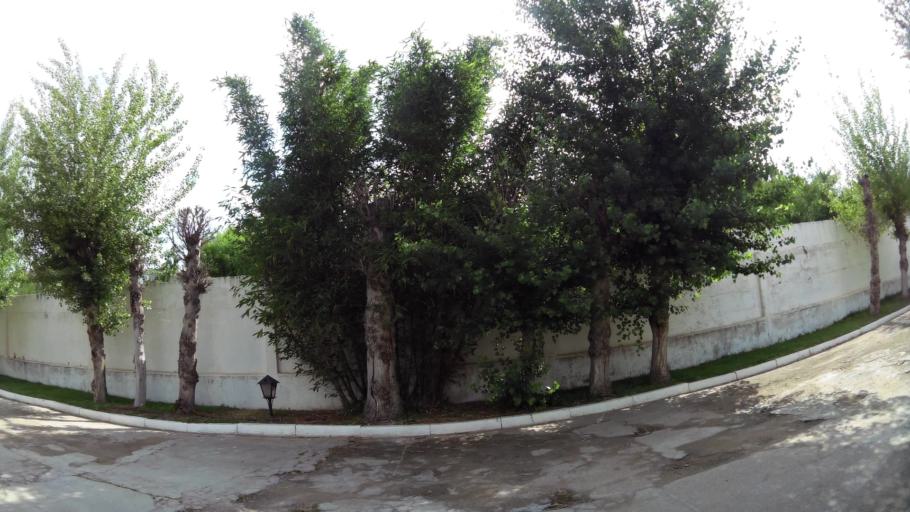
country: MA
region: Gharb-Chrarda-Beni Hssen
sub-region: Kenitra Province
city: Kenitra
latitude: 34.2803
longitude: -6.5366
